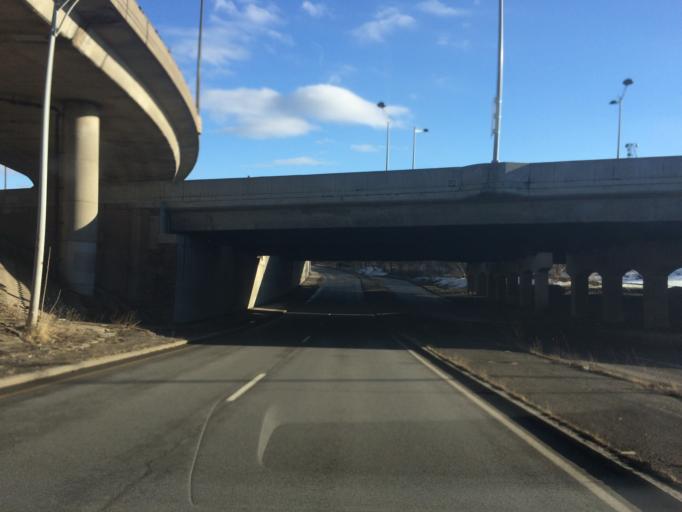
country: US
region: New York
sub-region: Monroe County
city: Rochester
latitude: 43.1516
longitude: -77.6074
